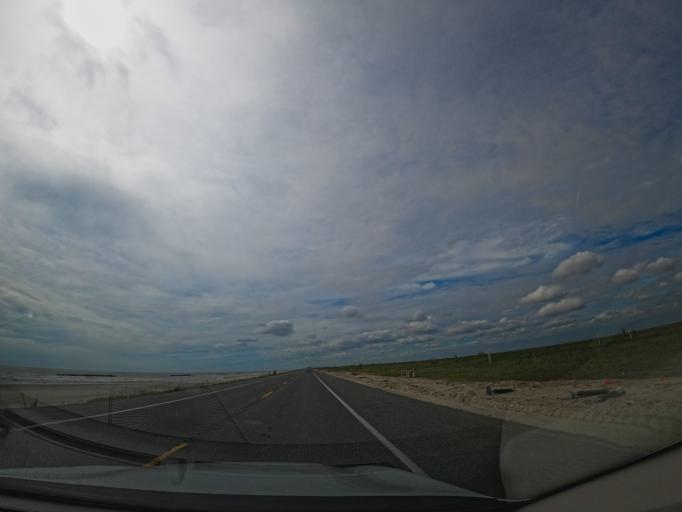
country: US
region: Louisiana
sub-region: Cameron Parish
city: Cameron
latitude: 29.7661
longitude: -93.5234
